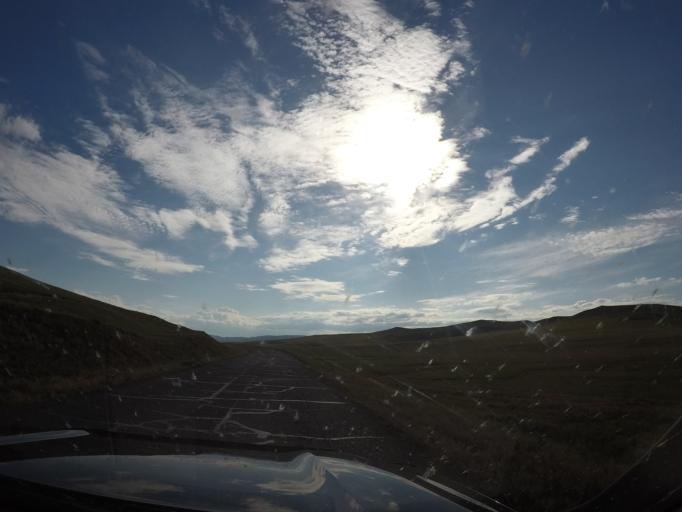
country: MN
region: Hentiy
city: Modot
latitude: 47.7859
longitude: 108.6689
